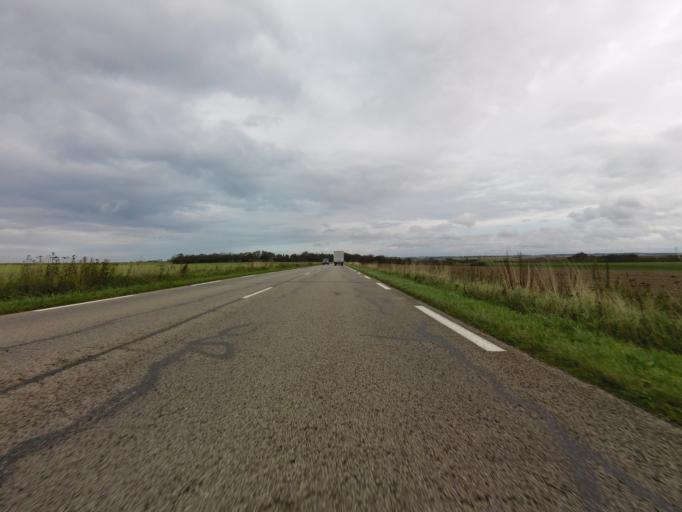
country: FR
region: Haute-Normandie
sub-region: Departement de la Seine-Maritime
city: Criel-sur-Mer
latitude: 49.9933
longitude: 1.2754
